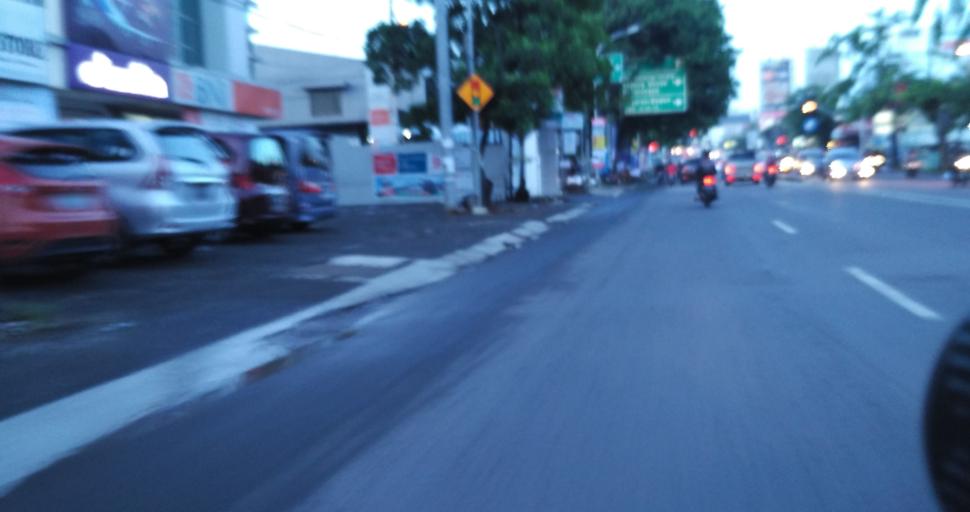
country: ID
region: Central Java
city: Semarang
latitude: -7.0498
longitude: 110.4189
